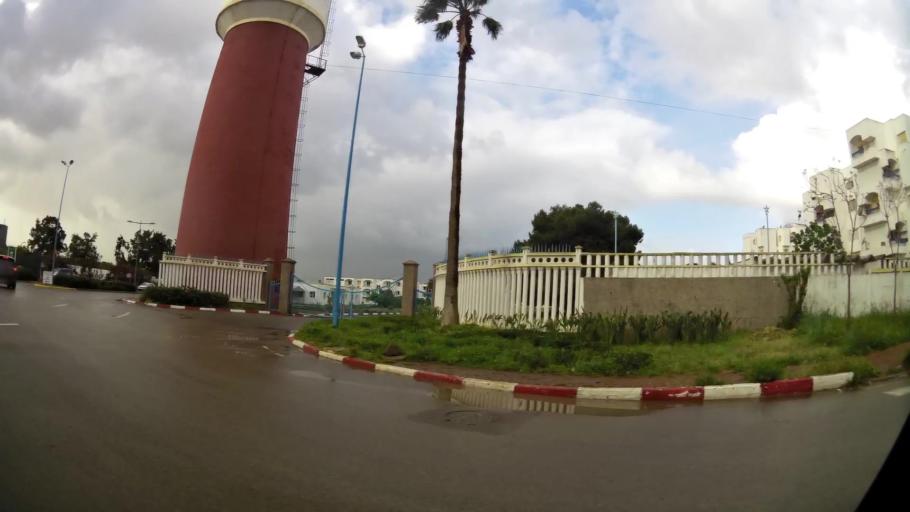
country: MA
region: Grand Casablanca
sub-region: Casablanca
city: Casablanca
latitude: 33.5559
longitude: -7.6509
